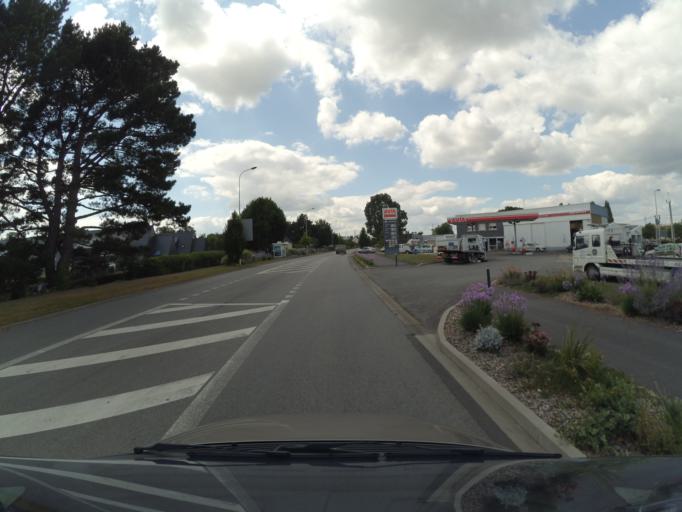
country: FR
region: Brittany
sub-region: Departement du Morbihan
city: Lanester
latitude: 47.7659
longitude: -3.3312
